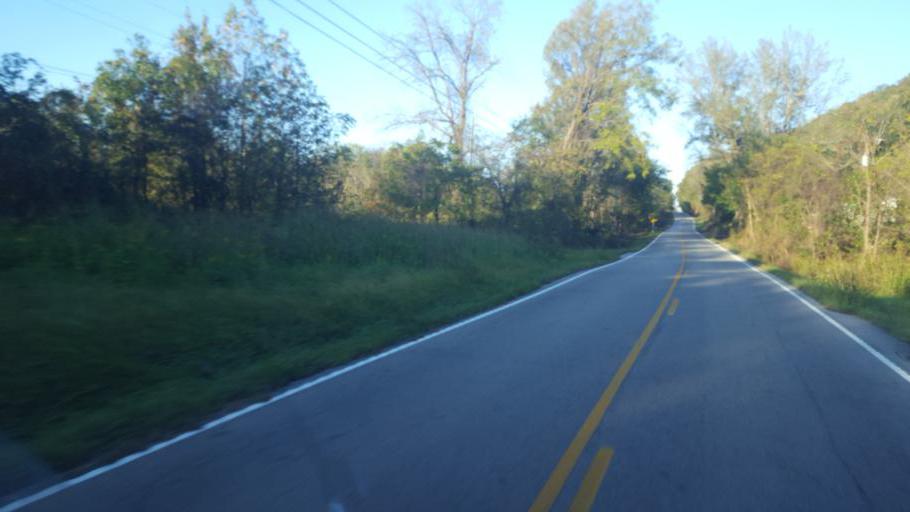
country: US
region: Ohio
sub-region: Scioto County
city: West Portsmouth
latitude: 38.6766
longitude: -83.0786
